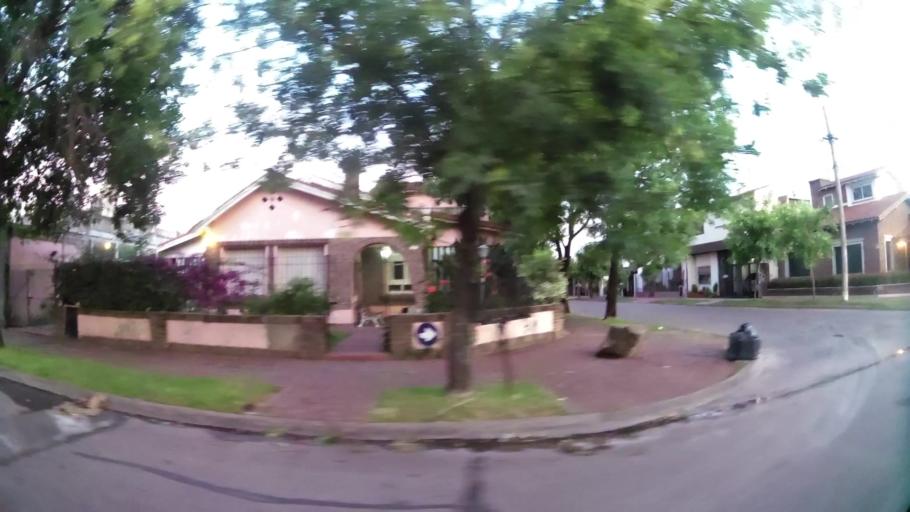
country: AR
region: Buenos Aires
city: Ituzaingo
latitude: -34.6556
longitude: -58.6400
